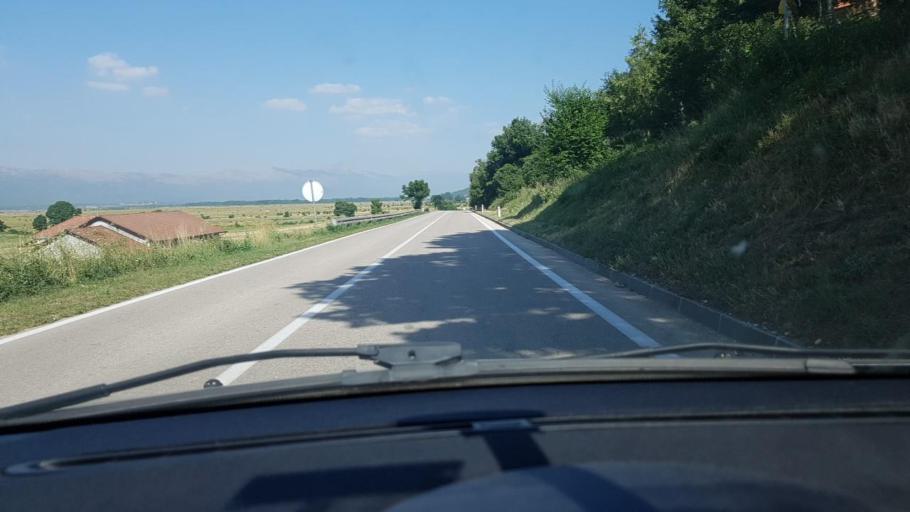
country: BA
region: Federation of Bosnia and Herzegovina
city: Orguz
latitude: 43.8735
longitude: 16.8701
